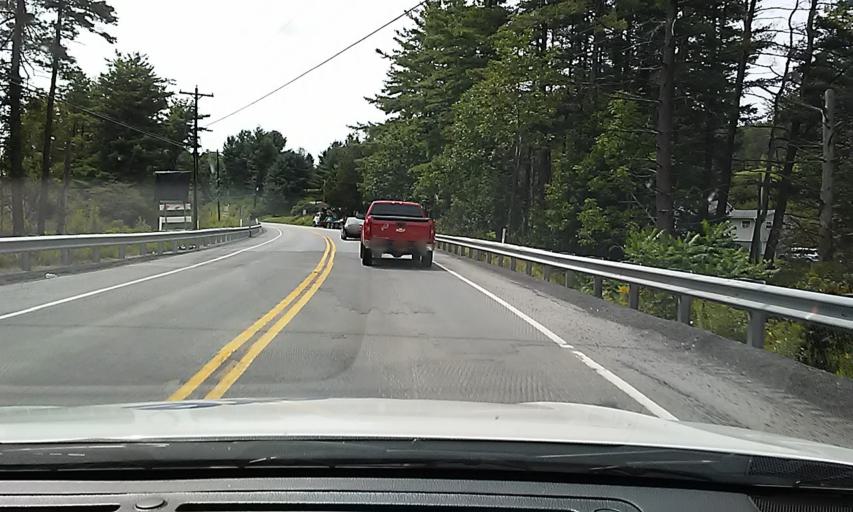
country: US
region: Pennsylvania
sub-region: Clearfield County
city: Treasure Lake
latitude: 41.1668
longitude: -78.6628
